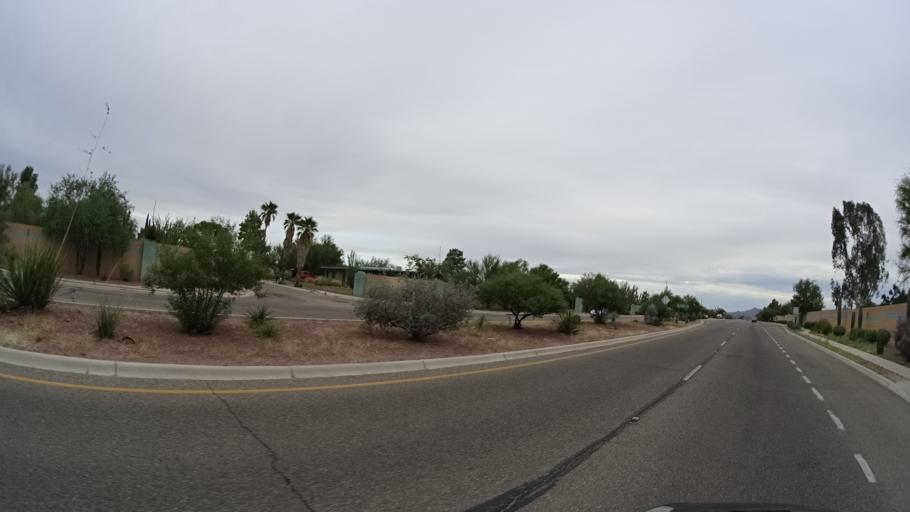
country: US
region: Arizona
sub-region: Pima County
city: Casas Adobes
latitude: 32.3466
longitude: -111.0470
